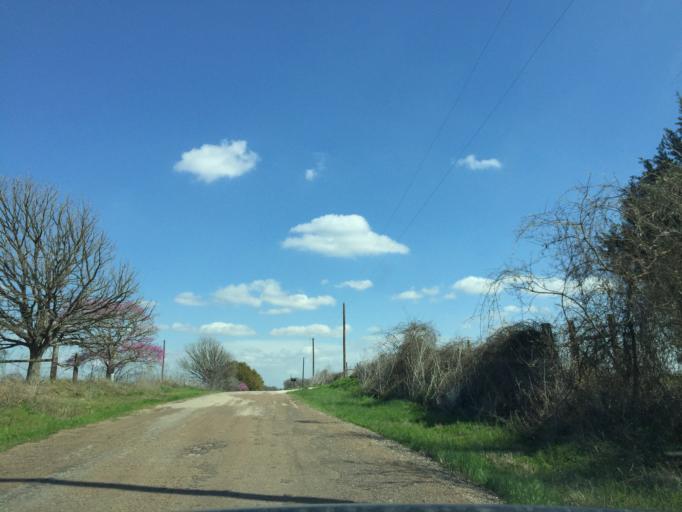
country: US
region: Texas
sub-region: Milam County
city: Thorndale
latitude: 30.5552
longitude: -97.1607
